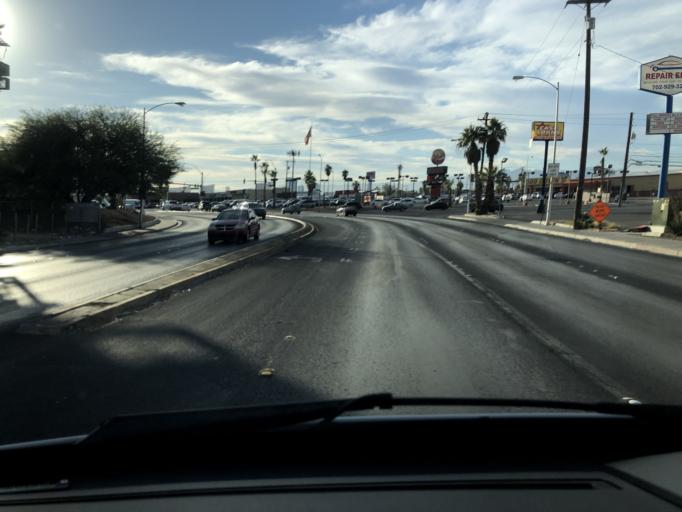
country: US
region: Nevada
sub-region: Clark County
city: Winchester
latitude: 36.1463
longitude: -115.0999
